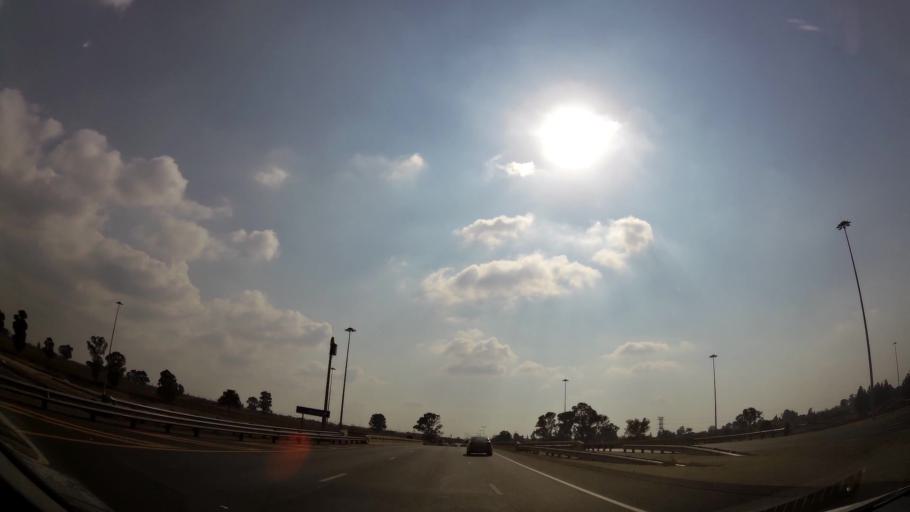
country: ZA
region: Gauteng
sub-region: Ekurhuleni Metropolitan Municipality
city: Brakpan
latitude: -26.1670
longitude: 28.3974
